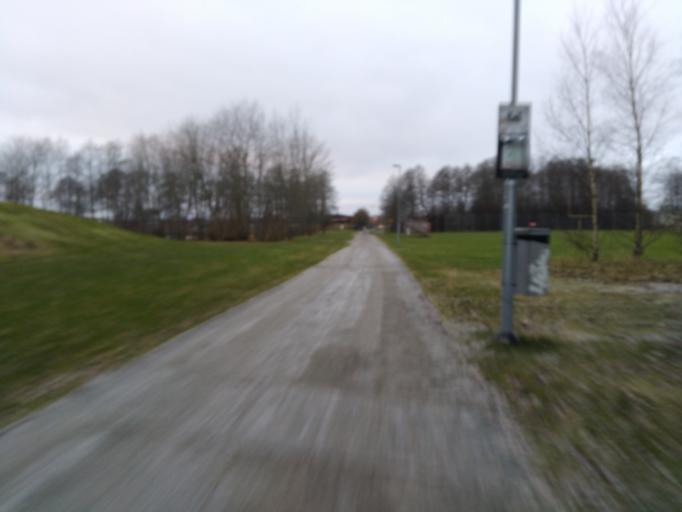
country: SE
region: Vaestra Goetaland
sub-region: Lidkopings Kommun
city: Lidkoping
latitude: 58.4925
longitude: 13.1779
